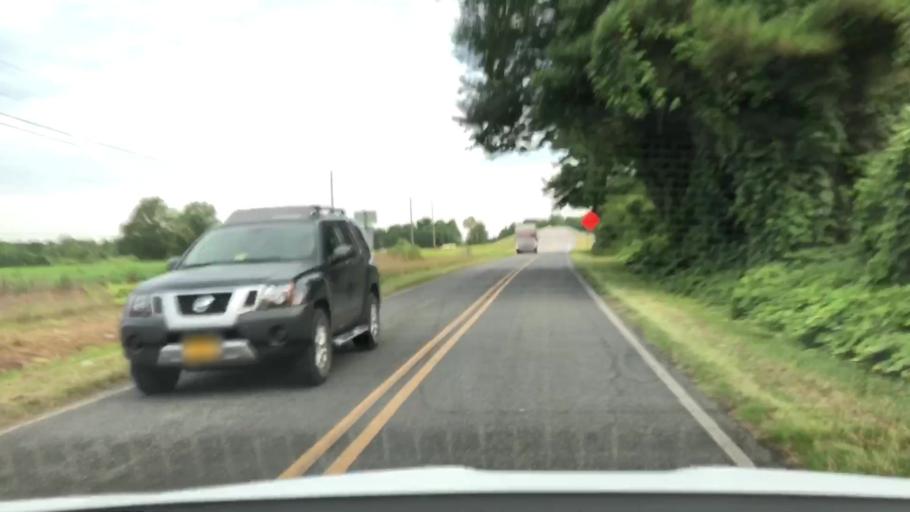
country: US
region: North Carolina
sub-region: Jones County
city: Maysville
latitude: 34.9091
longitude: -77.2354
